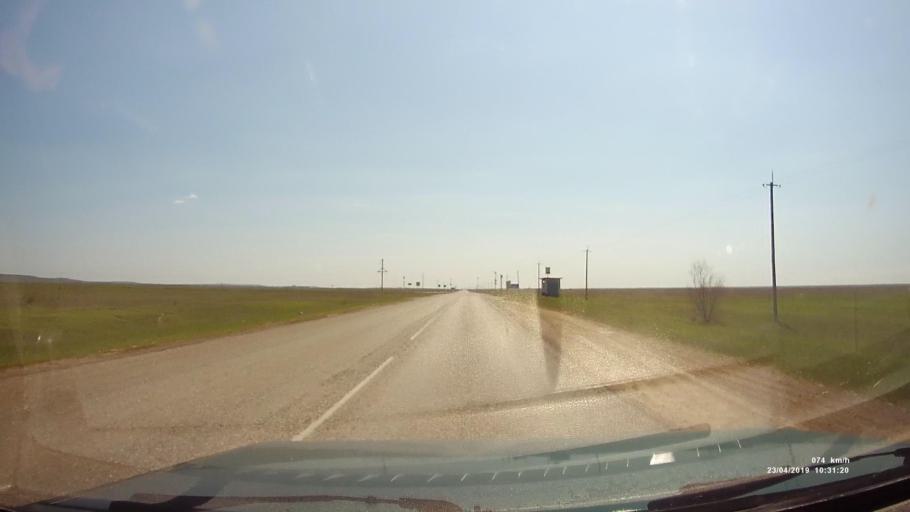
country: RU
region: Kalmykiya
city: Yashalta
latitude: 46.5865
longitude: 42.5602
